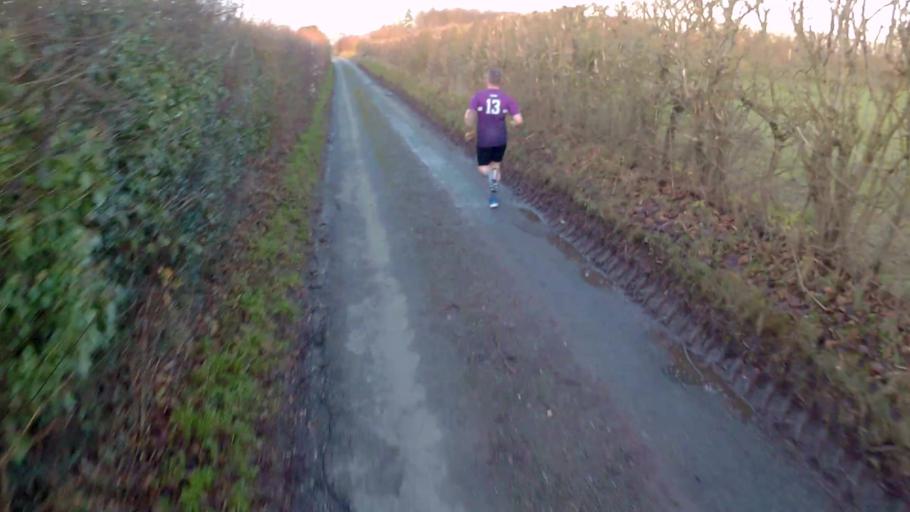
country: GB
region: England
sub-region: Hampshire
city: Overton
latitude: 51.2189
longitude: -1.2437
